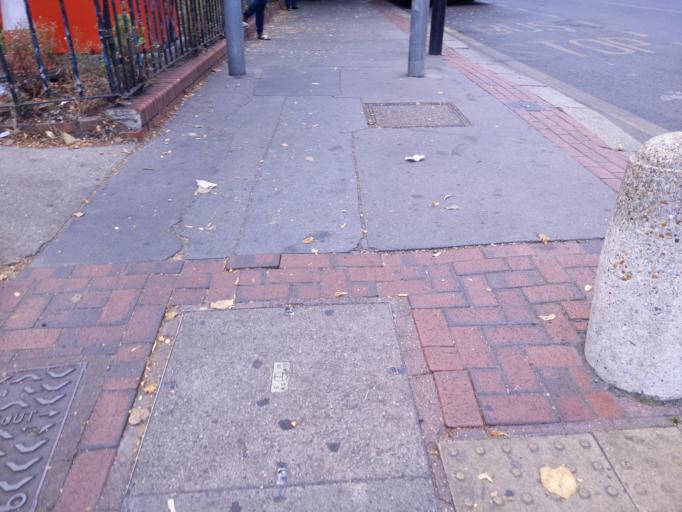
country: GB
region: England
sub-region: Greater London
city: Thornton Heath
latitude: 51.3926
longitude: -0.1139
